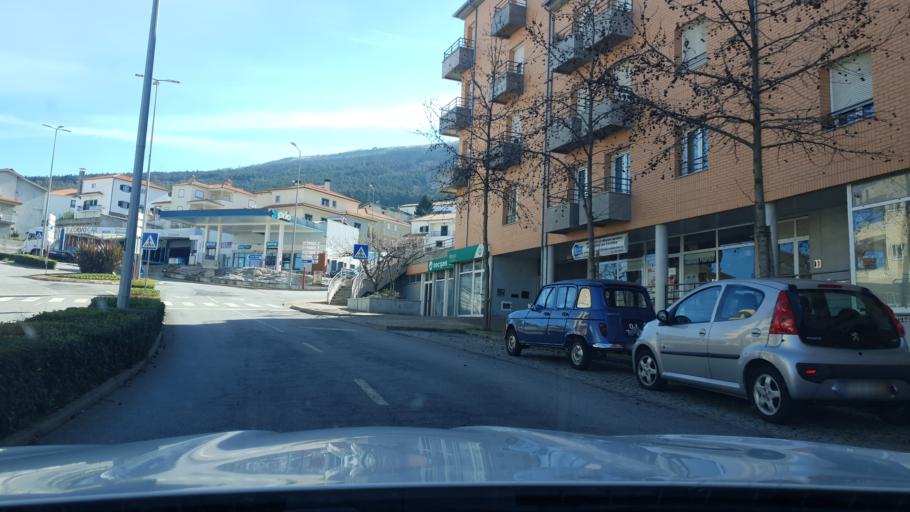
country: PT
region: Braganca
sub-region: Torre de Moncorvo
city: Torre de Moncorvo
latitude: 41.1746
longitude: -7.0496
